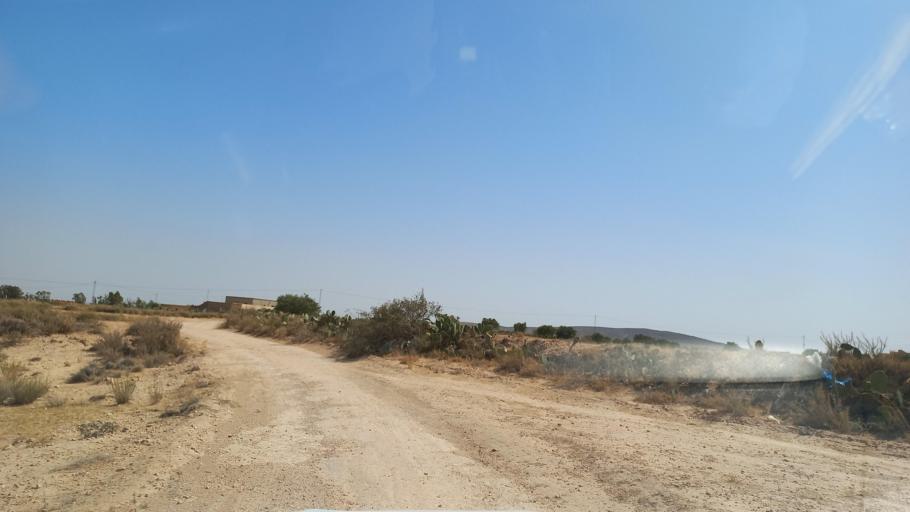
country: TN
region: Al Qasrayn
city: Kasserine
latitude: 35.2205
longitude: 9.0357
